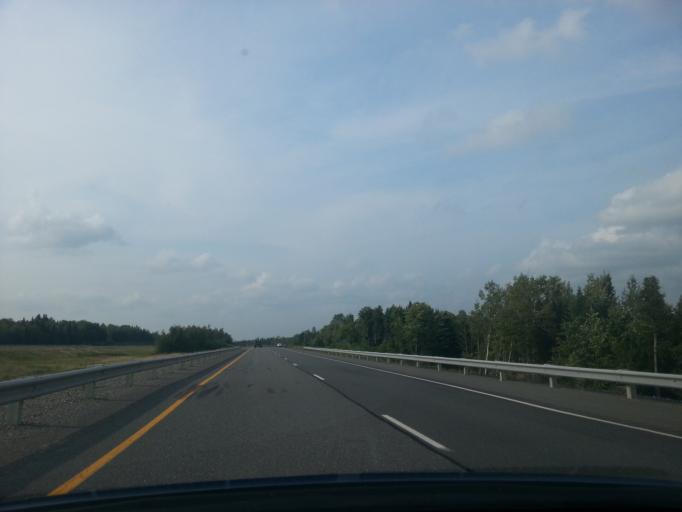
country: CA
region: New Brunswick
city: Florenceville-Bristol
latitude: 46.3567
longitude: -67.6136
